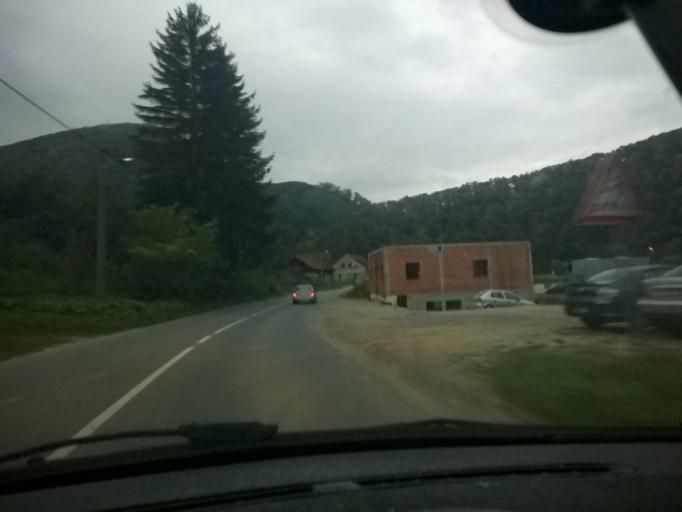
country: HR
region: Krapinsko-Zagorska
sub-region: Grad Krapina
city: Krapina
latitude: 46.1801
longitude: 15.8541
